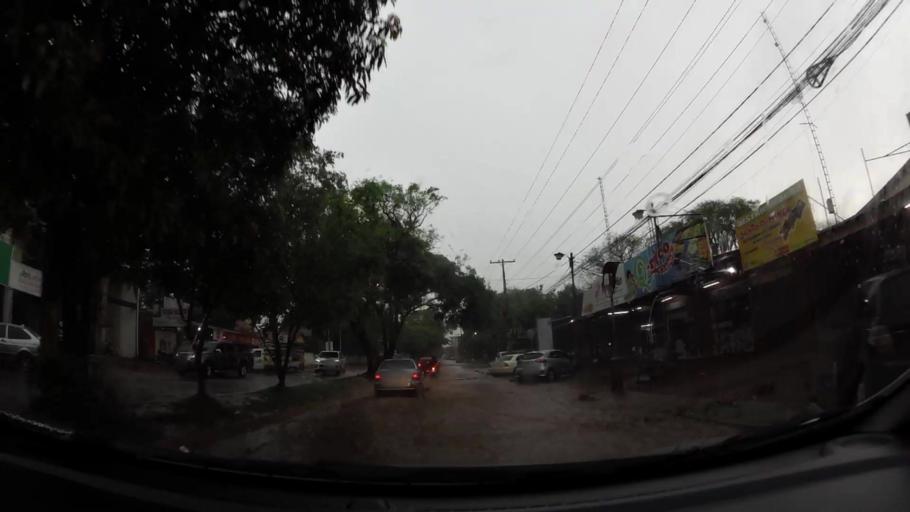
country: PY
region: Alto Parana
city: Ciudad del Este
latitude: -25.5021
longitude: -54.6679
